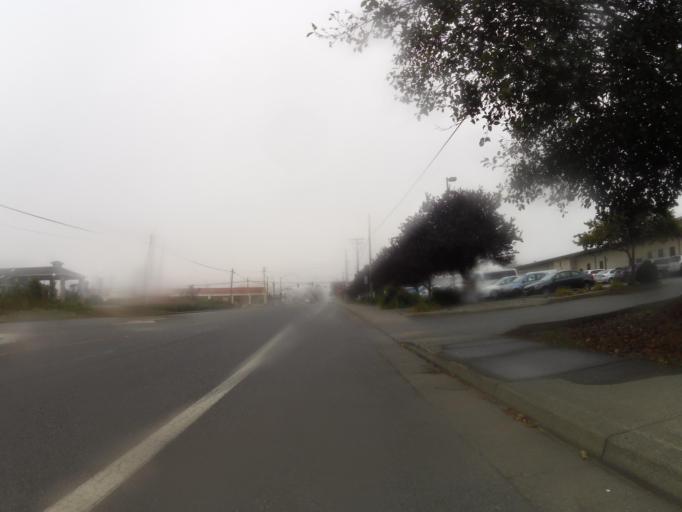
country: US
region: California
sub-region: Del Norte County
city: Crescent City
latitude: 41.7728
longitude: -124.1982
